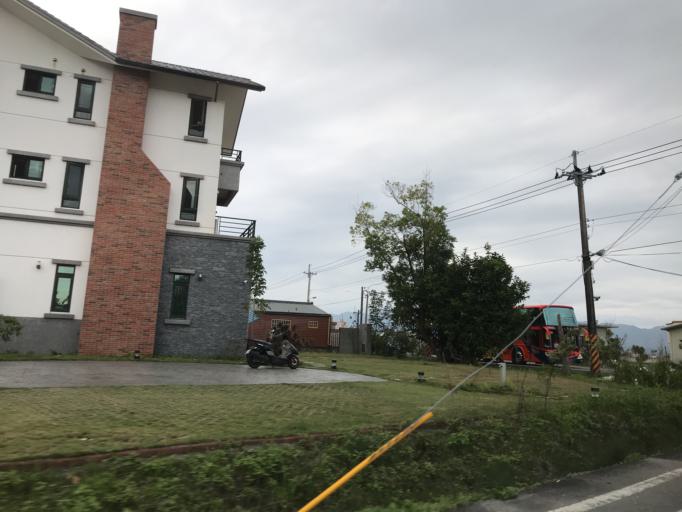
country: TW
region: Taiwan
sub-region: Yilan
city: Yilan
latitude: 24.6899
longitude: 121.7866
